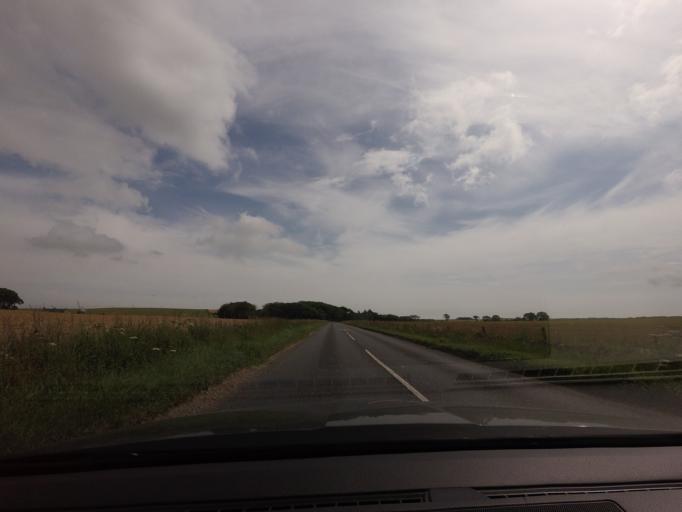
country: GB
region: Scotland
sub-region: Aberdeenshire
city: Mintlaw
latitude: 57.5129
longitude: -1.9267
